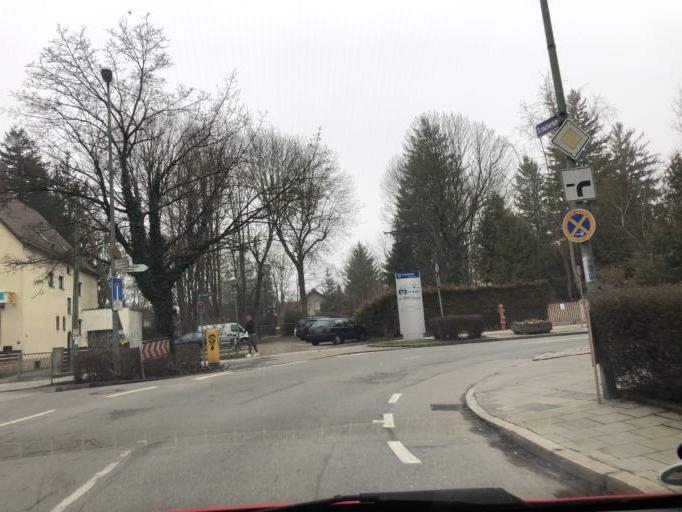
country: DE
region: Bavaria
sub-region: Upper Bavaria
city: Grobenzell
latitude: 48.1970
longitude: 11.3736
